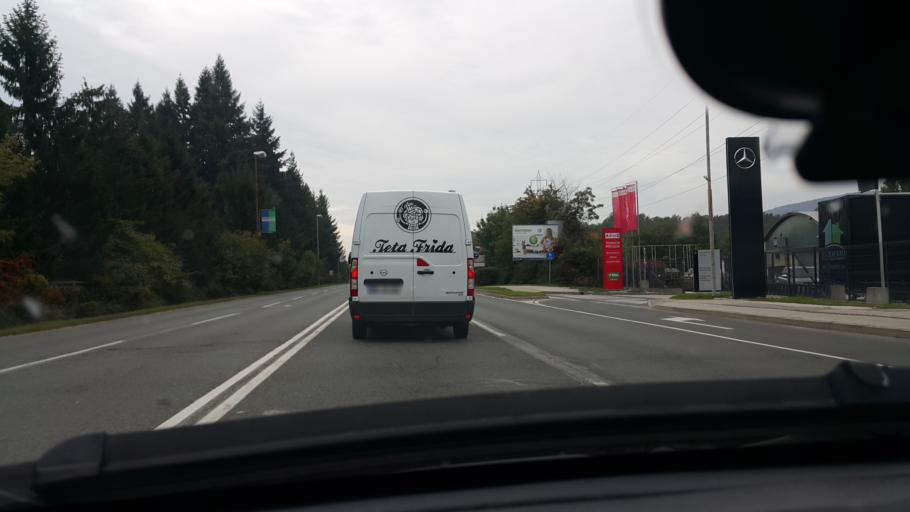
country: SI
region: Maribor
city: Maribor
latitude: 46.5368
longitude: 15.6463
